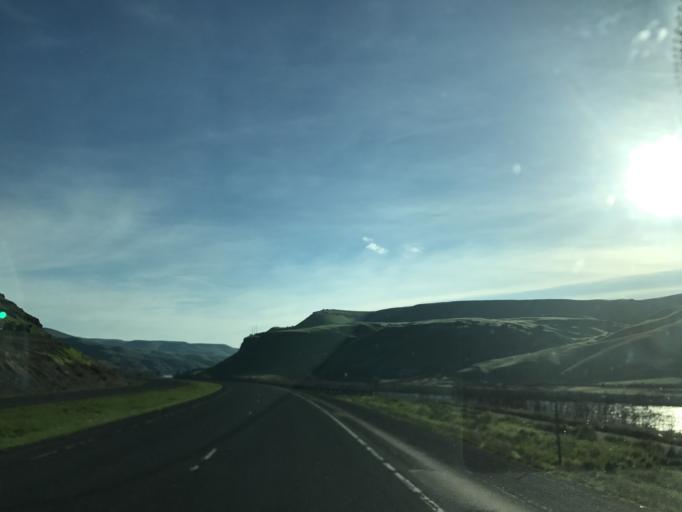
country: US
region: Idaho
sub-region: Nez Perce County
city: Lewiston Orchards
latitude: 46.4268
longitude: -116.9202
